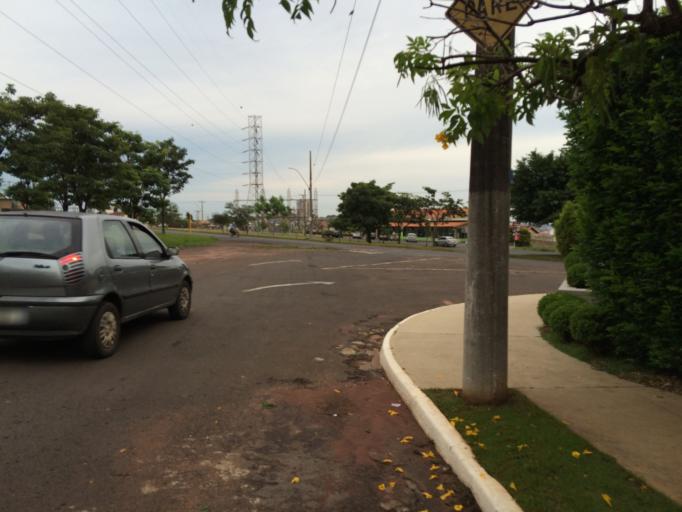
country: BR
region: Sao Paulo
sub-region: Matao
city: Matao
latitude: -21.6173
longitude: -48.3637
